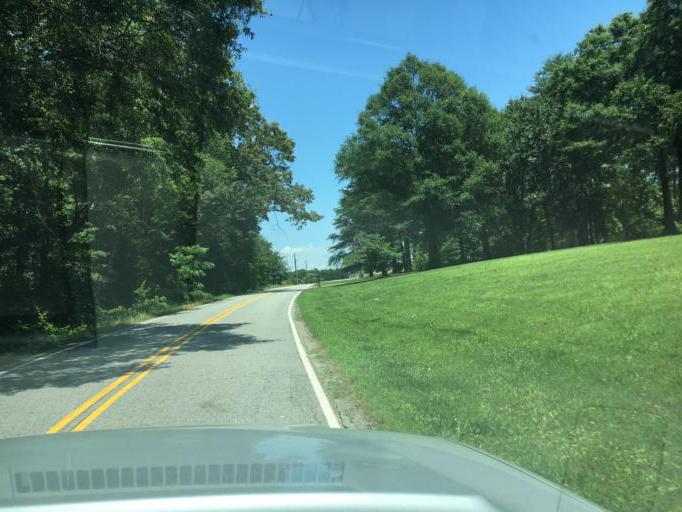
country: US
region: South Carolina
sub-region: Greenville County
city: Greer
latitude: 34.9630
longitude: -82.1964
